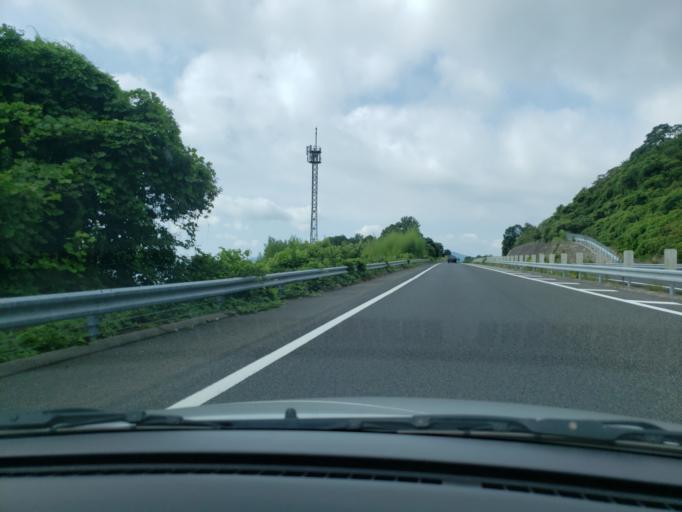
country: JP
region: Hiroshima
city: Innoshima
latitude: 34.2784
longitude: 133.1086
